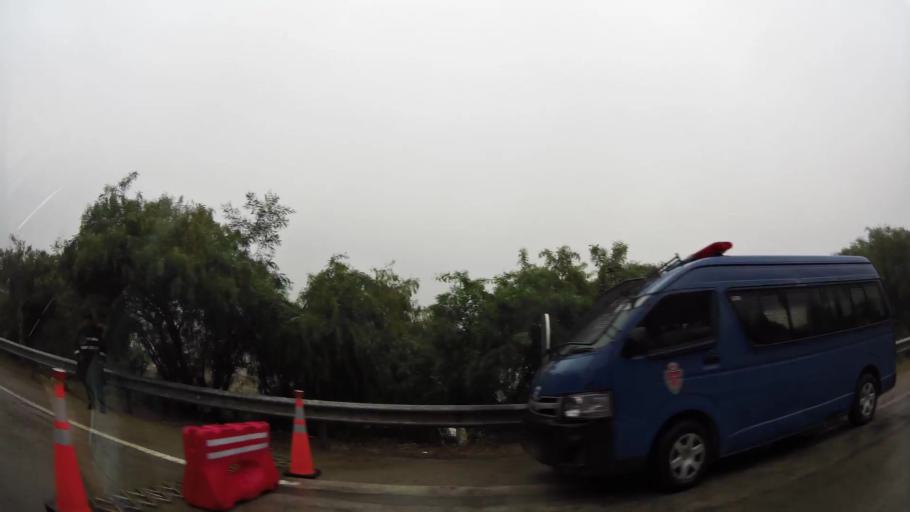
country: MA
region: Taza-Al Hoceima-Taounate
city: Tirhanimine
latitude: 35.2215
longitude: -3.9268
